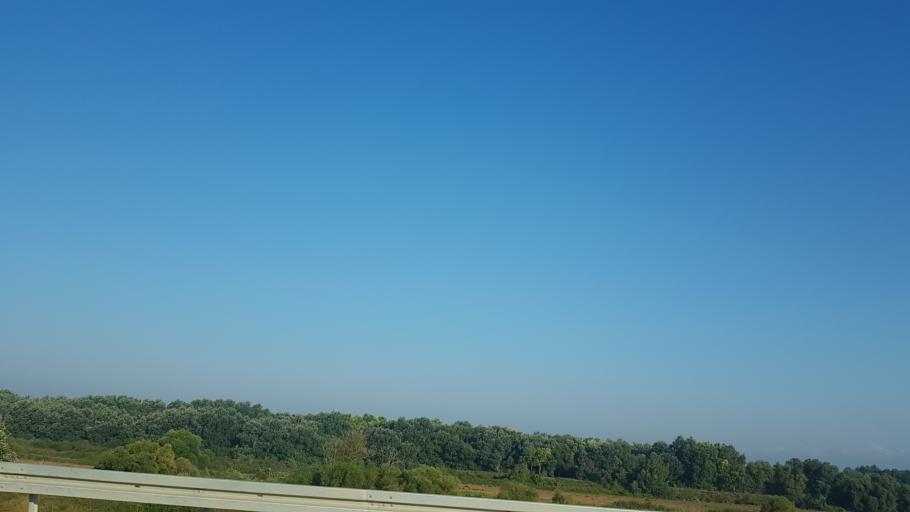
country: TR
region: Bursa
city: Karacabey
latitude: 40.1643
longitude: 28.3180
